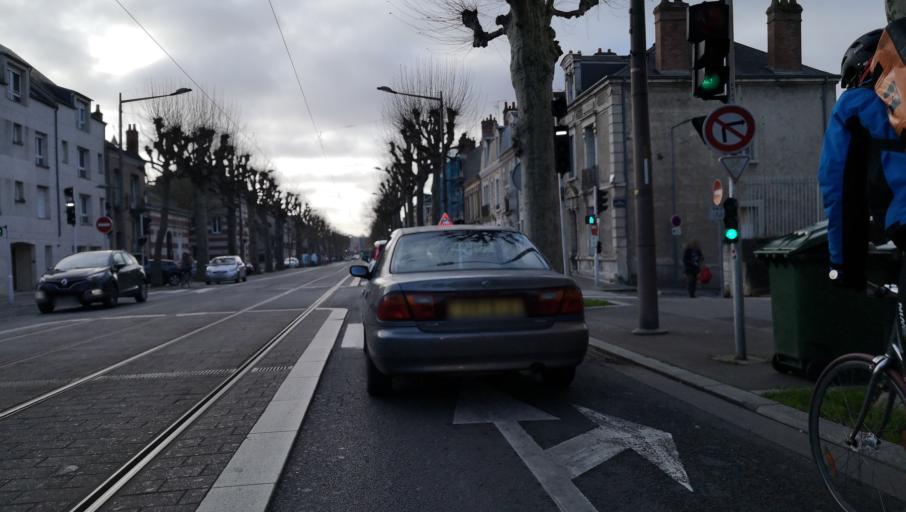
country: FR
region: Centre
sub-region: Departement du Loiret
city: Saint-Jean-le-Blanc
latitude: 47.8917
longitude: 1.9047
